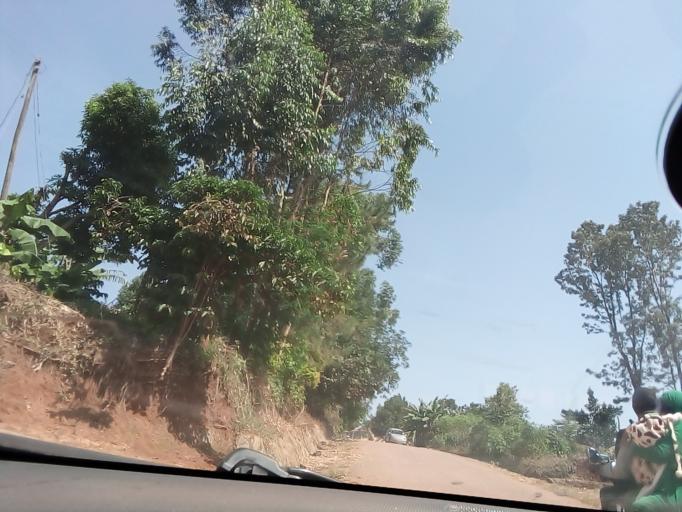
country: UG
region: Central Region
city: Masaka
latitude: -0.3480
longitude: 31.7435
